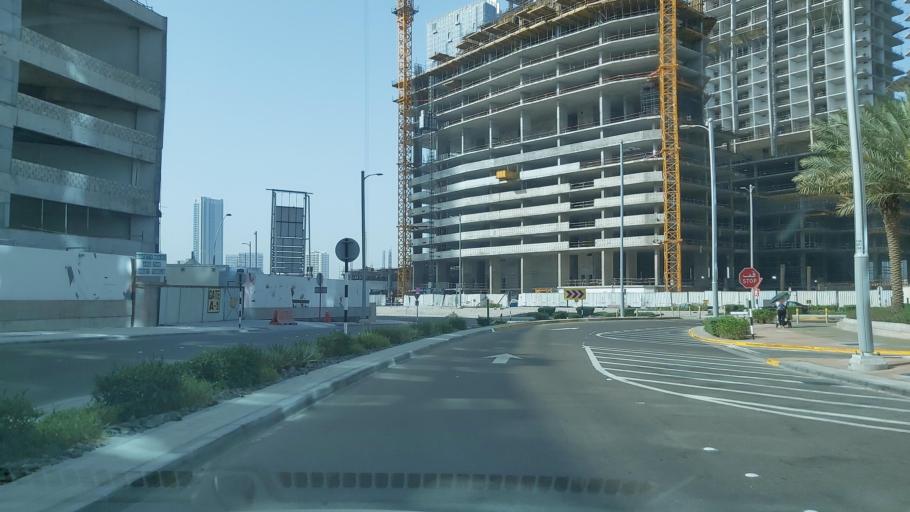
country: AE
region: Abu Dhabi
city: Abu Dhabi
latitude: 24.4982
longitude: 54.4055
